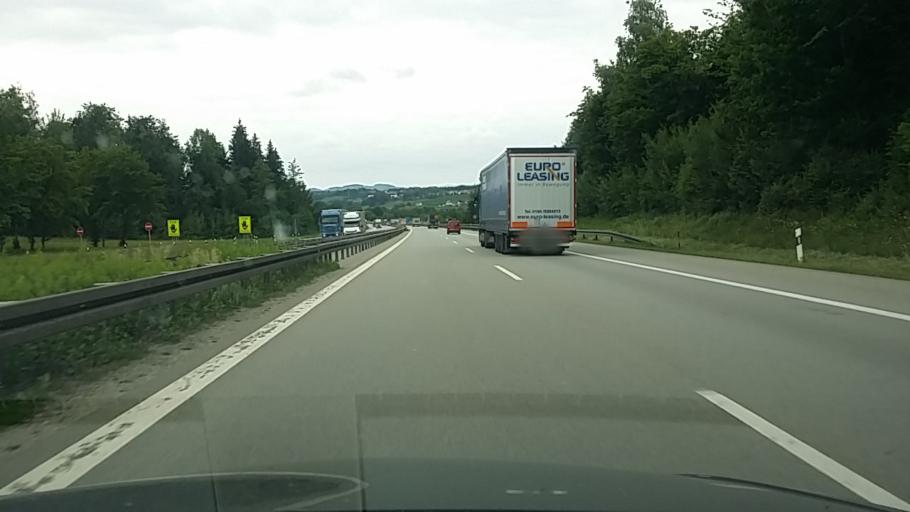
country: DE
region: Bavaria
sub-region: Lower Bavaria
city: Passau
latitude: 48.5587
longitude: 13.3898
